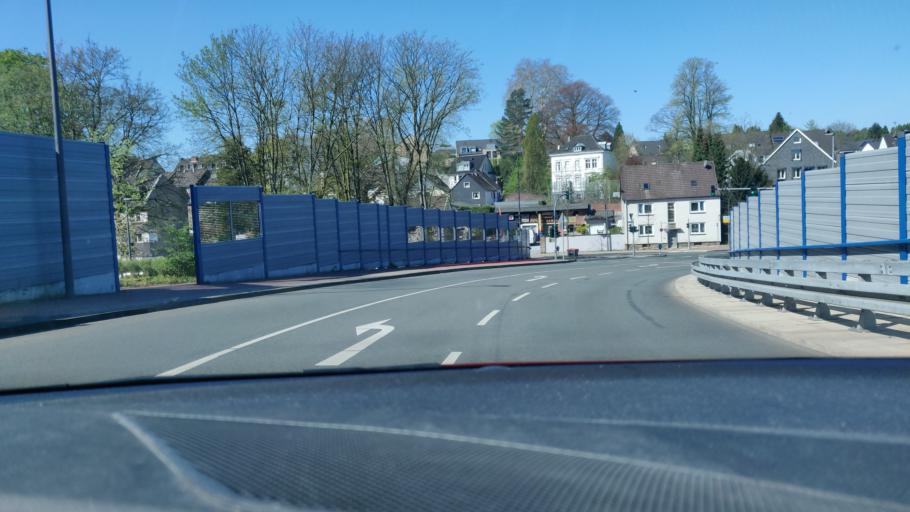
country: DE
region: North Rhine-Westphalia
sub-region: Regierungsbezirk Dusseldorf
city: Mettmann
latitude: 51.2540
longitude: 6.9795
